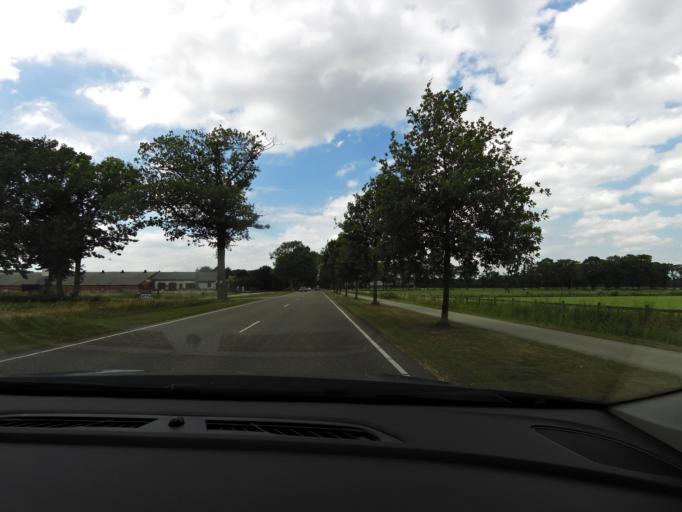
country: NL
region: North Brabant
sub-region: Gemeente Baarle-Nassau
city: Baarle-Nassau
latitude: 51.4645
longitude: 4.9067
